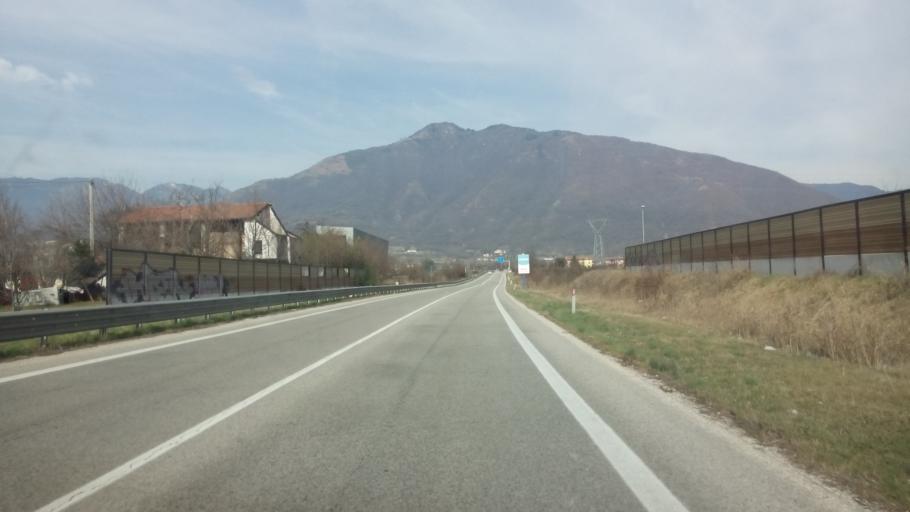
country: IT
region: Veneto
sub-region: Provincia di Vicenza
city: Zane
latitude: 45.7205
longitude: 11.4248
